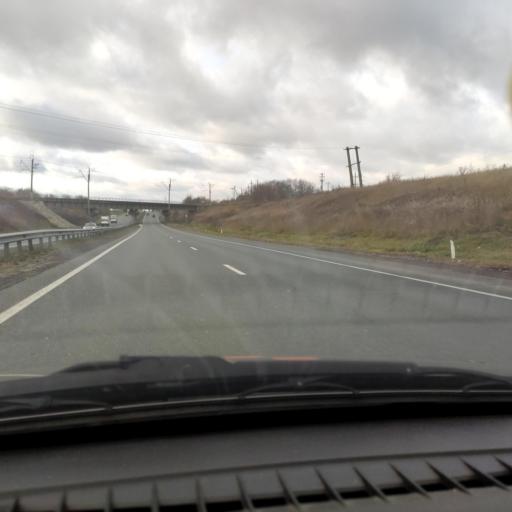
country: RU
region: Samara
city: Tol'yatti
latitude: 53.5684
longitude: 49.4853
